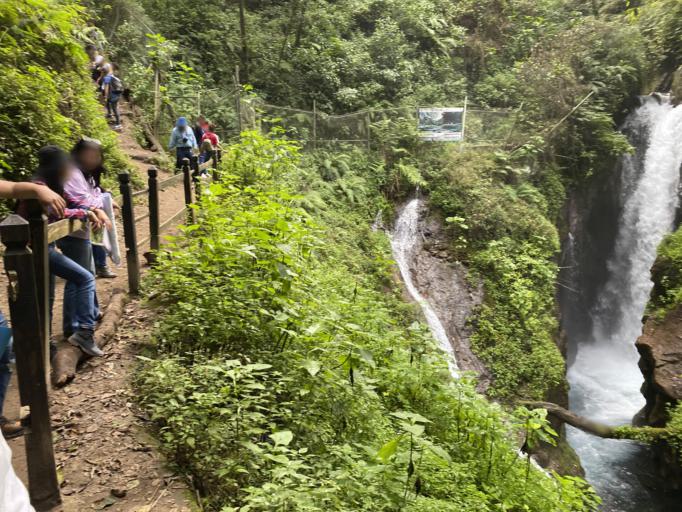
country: MX
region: Veracruz
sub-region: Altotonga
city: Adolfo Moreno
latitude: 19.7380
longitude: -97.2523
